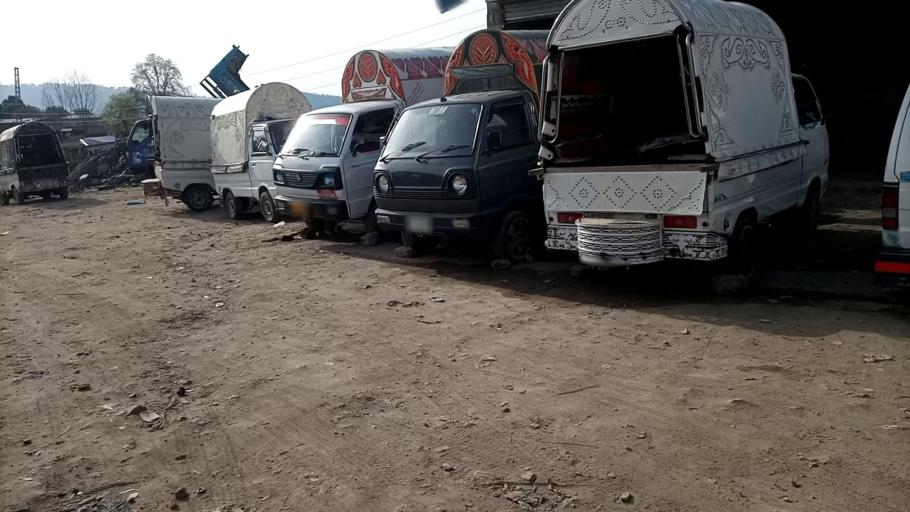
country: PK
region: Khyber Pakhtunkhwa
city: Abbottabad
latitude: 34.2198
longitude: 73.2445
